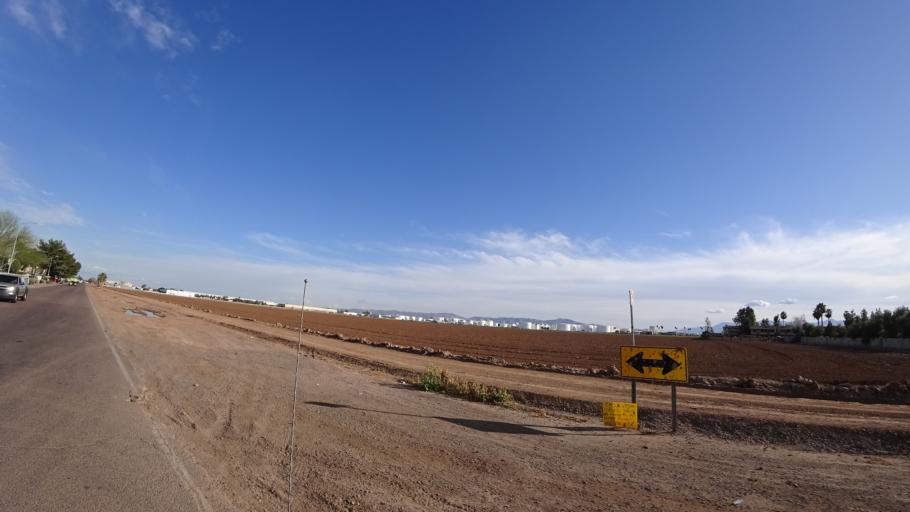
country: US
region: Arizona
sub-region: Maricopa County
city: Tolleson
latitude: 33.4588
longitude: -112.1824
